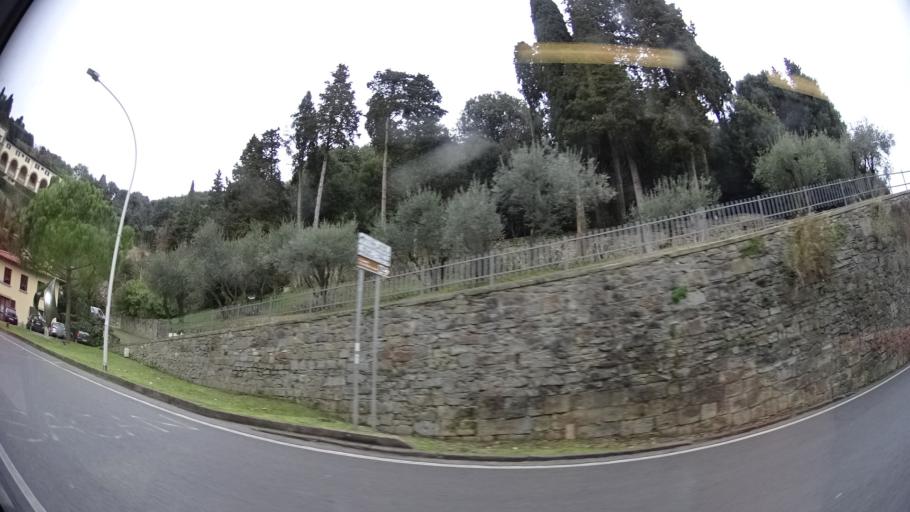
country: IT
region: Tuscany
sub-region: Province of Florence
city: Fiesole
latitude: 43.8035
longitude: 11.2957
